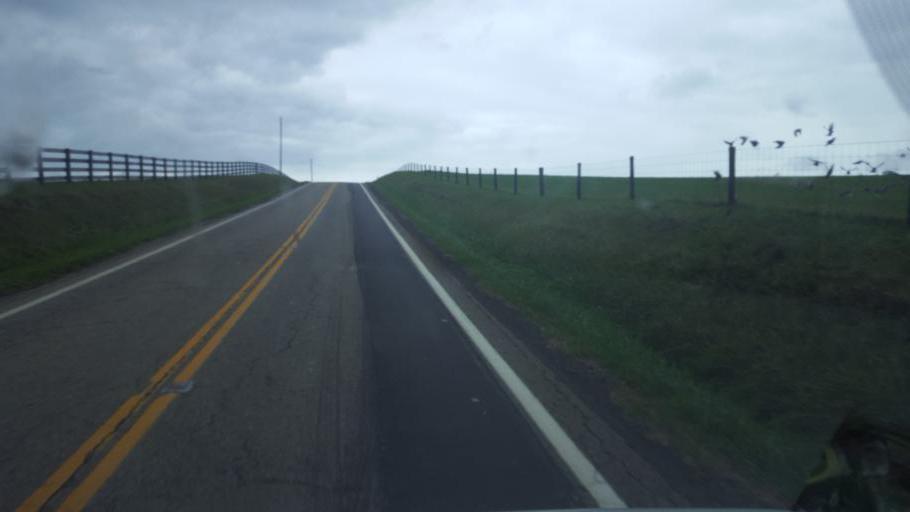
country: US
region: Ohio
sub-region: Ashland County
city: Loudonville
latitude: 40.5570
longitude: -82.1638
